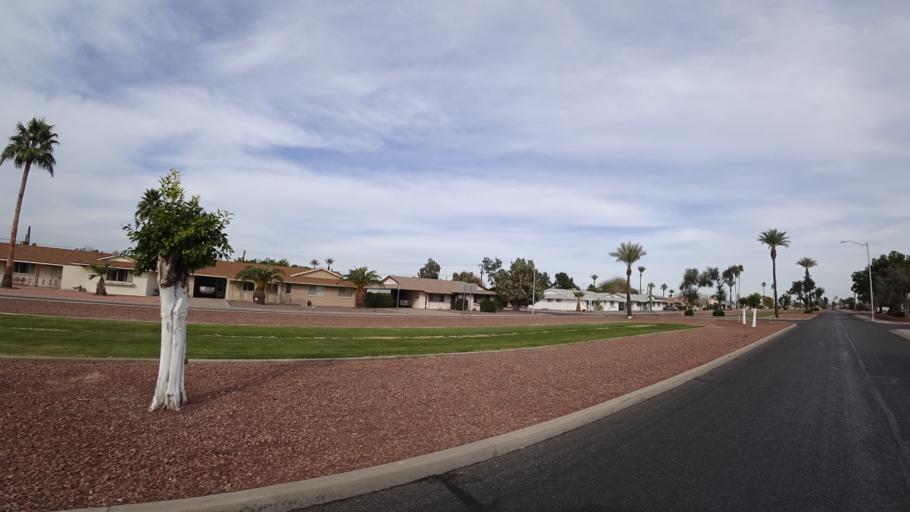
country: US
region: Arizona
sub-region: Maricopa County
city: Sun City
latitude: 33.5801
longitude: -112.2789
